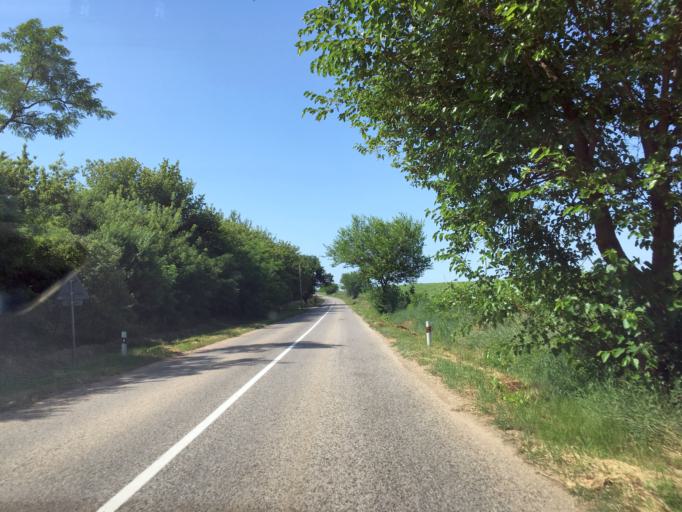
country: SK
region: Nitriansky
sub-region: Okres Komarno
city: Hurbanovo
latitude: 47.8747
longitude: 18.2845
